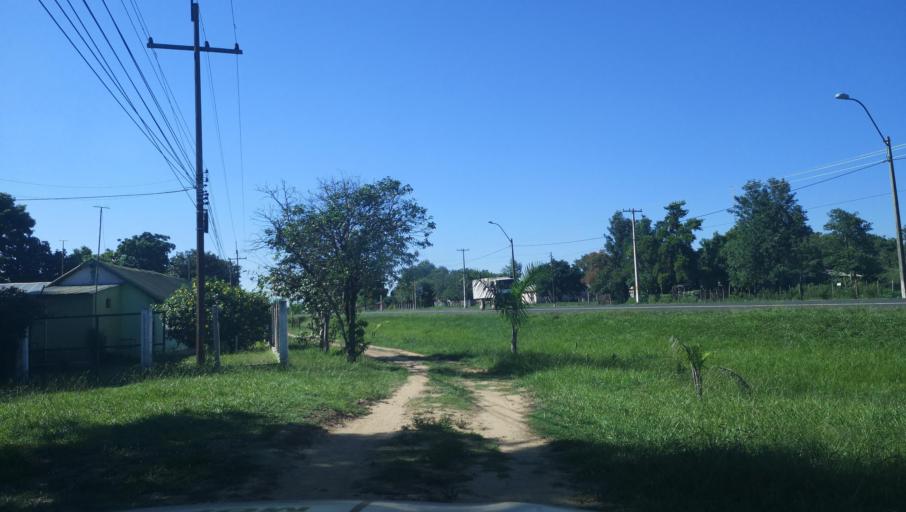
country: PY
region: Caaguazu
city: Carayao
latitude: -25.2071
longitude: -56.3989
